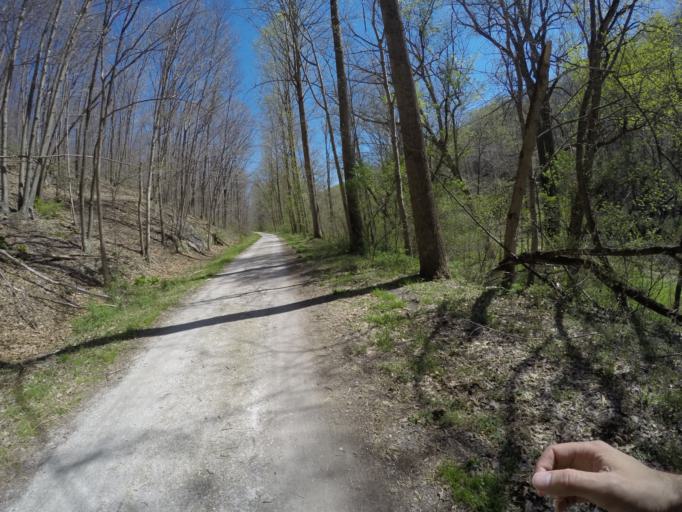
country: US
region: Maryland
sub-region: Baltimore County
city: Hunt Valley
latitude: 39.5954
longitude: -76.6225
